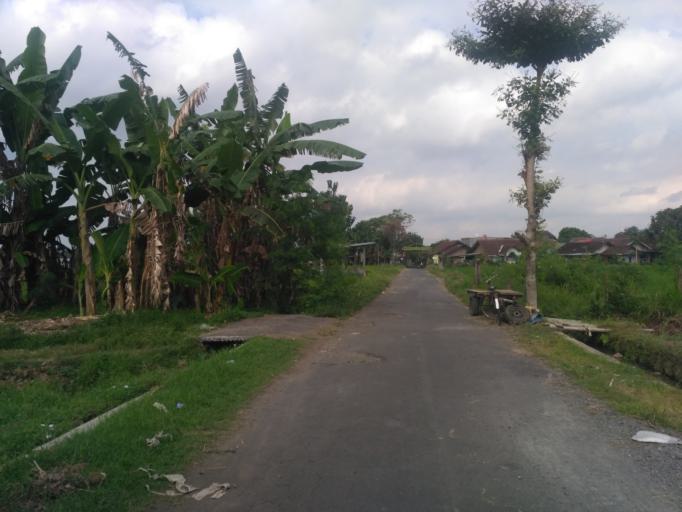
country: ID
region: Daerah Istimewa Yogyakarta
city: Yogyakarta
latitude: -7.7604
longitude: 110.3541
